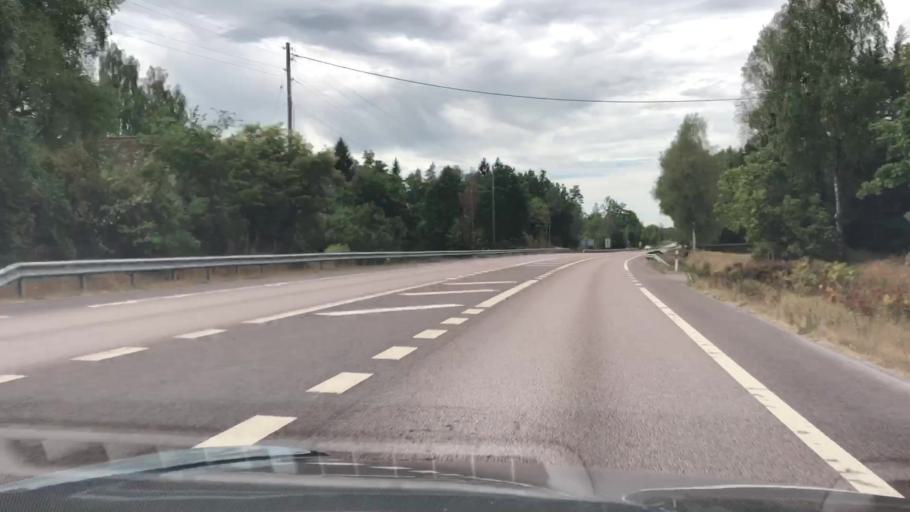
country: SE
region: Kalmar
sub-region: Torsas Kommun
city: Torsas
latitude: 56.2799
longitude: 15.9761
